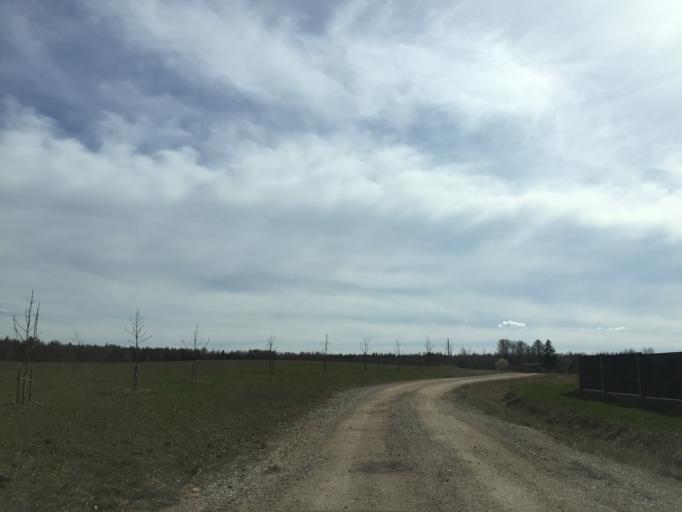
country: LV
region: Ikskile
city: Ikskile
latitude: 56.8419
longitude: 24.5304
